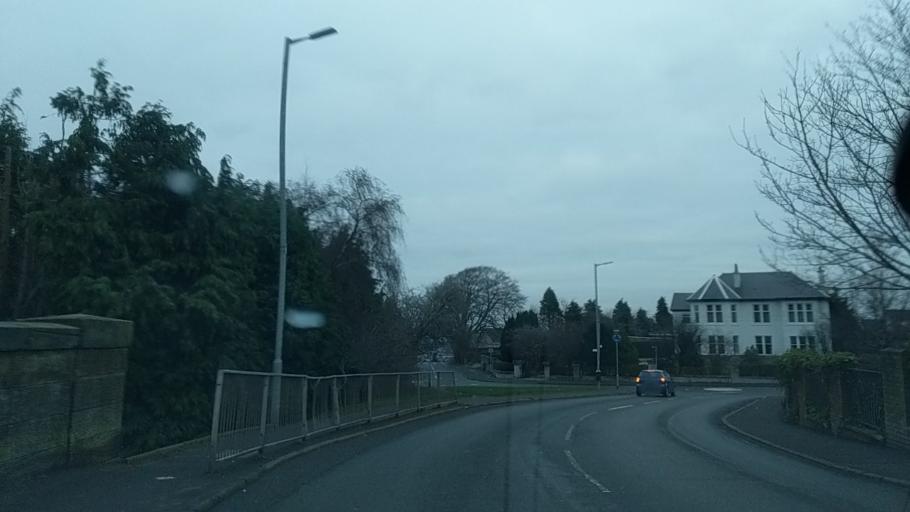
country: GB
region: Scotland
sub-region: South Lanarkshire
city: Rutherglen
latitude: 55.8153
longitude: -4.1875
